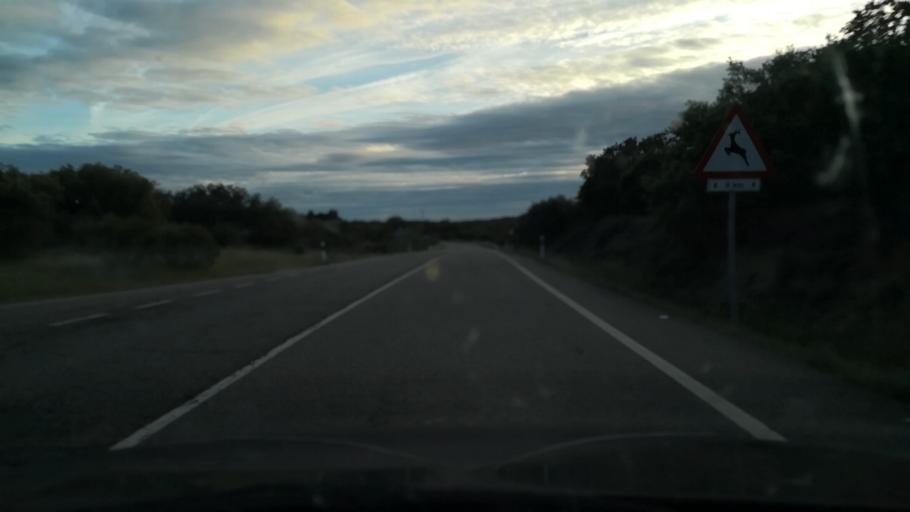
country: ES
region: Extremadura
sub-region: Provincia de Badajoz
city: La Roca de la Sierra
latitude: 39.1374
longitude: -6.6581
